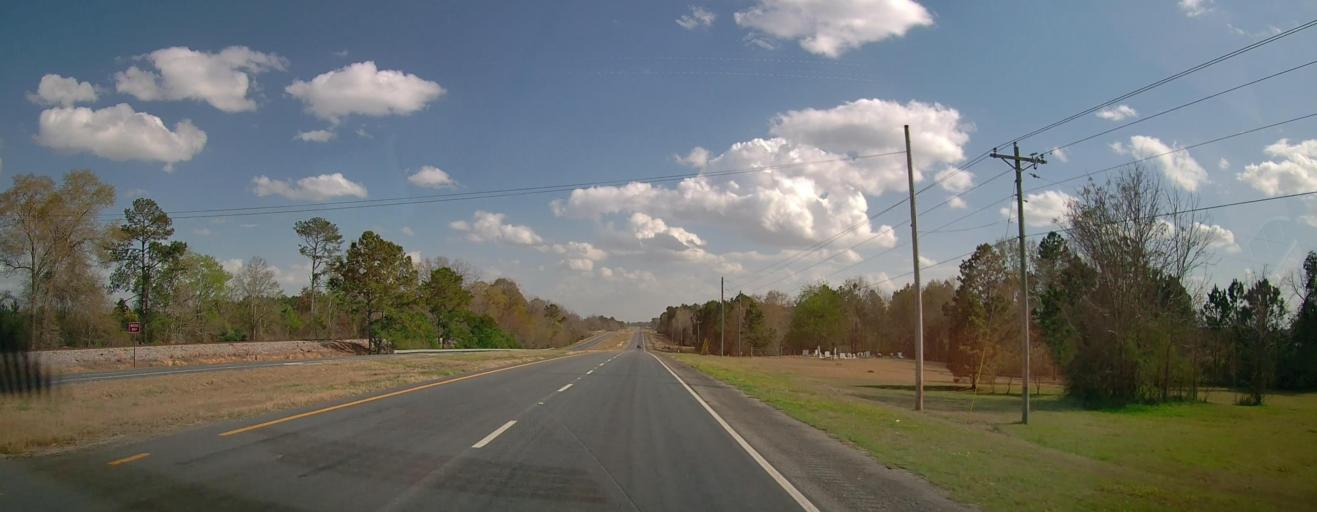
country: US
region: Georgia
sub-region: Dodge County
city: Eastman
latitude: 32.1427
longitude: -83.1335
